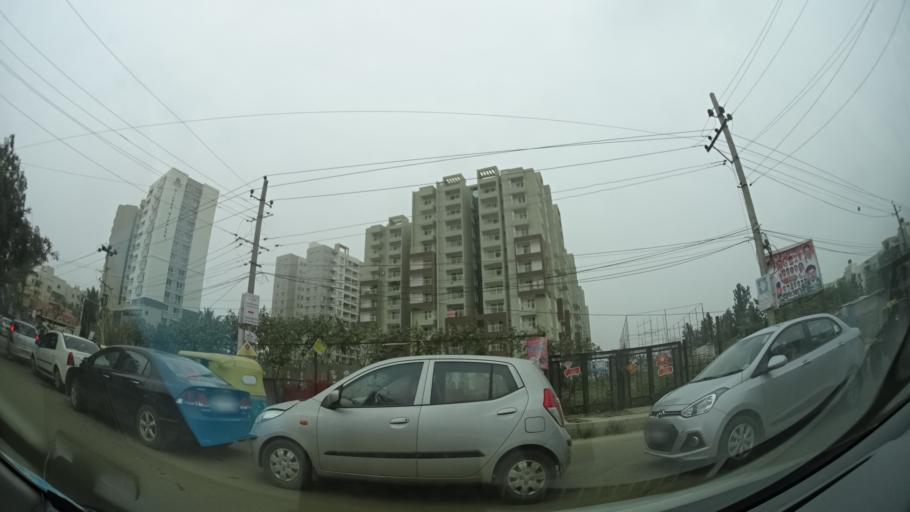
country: IN
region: Karnataka
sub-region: Bangalore Rural
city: Hoskote
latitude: 12.9690
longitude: 77.7397
